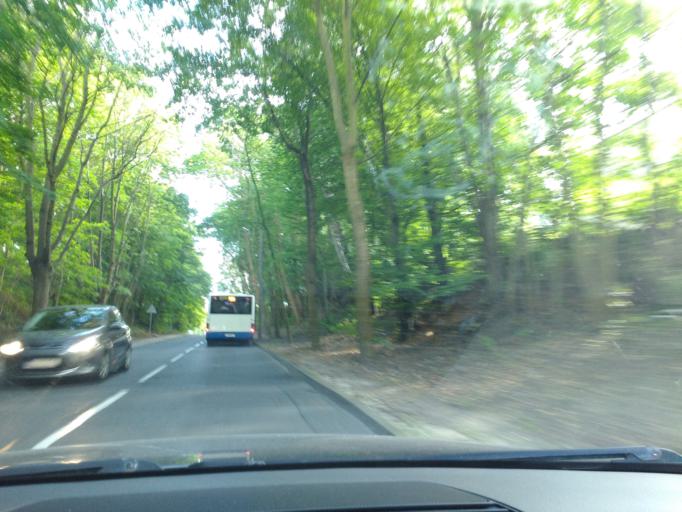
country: PL
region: Pomeranian Voivodeship
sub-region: Gdynia
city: Gdynia
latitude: 54.5037
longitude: 18.5138
